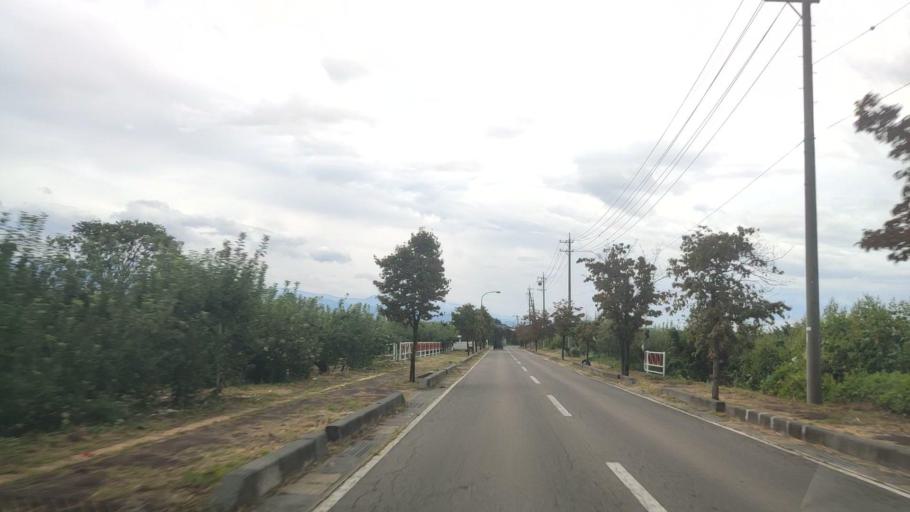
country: JP
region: Nagano
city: Nakano
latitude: 36.7847
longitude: 138.3561
